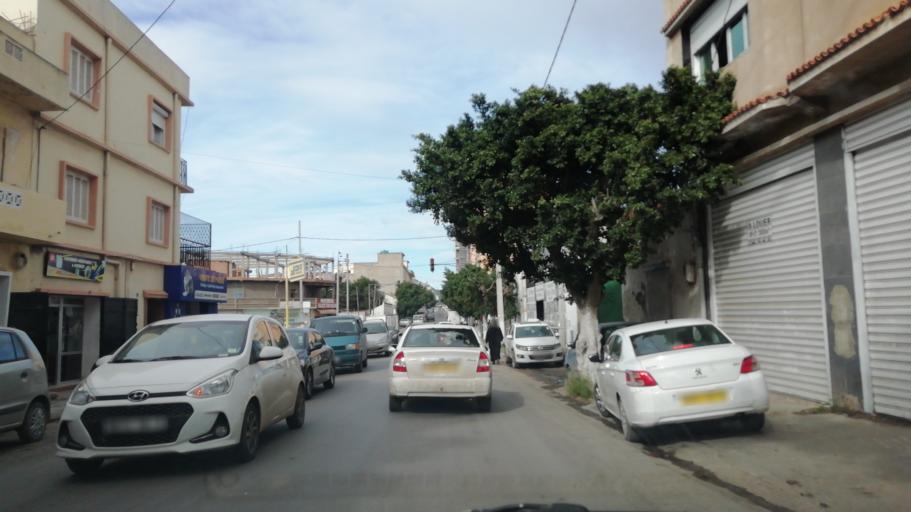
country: DZ
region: Oran
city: Oran
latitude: 35.6893
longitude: -0.6240
